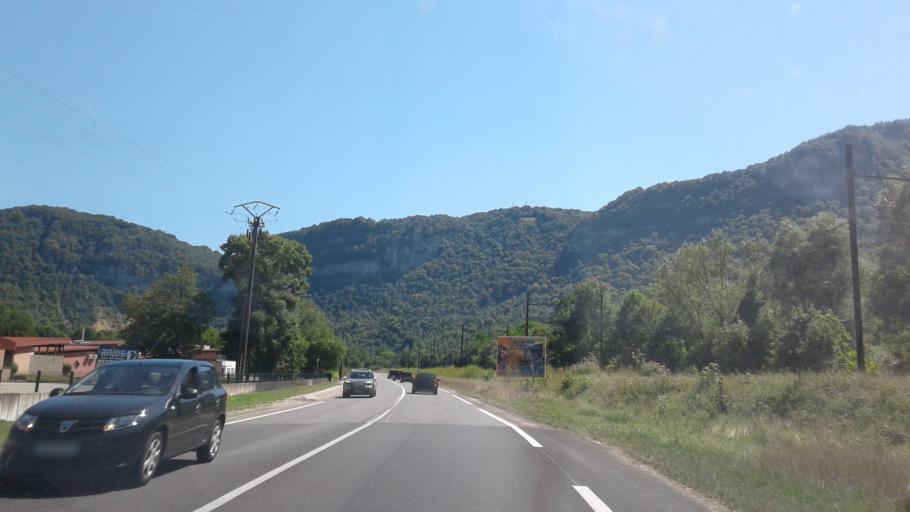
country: FR
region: Rhone-Alpes
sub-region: Departement de l'Ain
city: Vaux-en-Bugey
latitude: 45.9254
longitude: 5.3893
